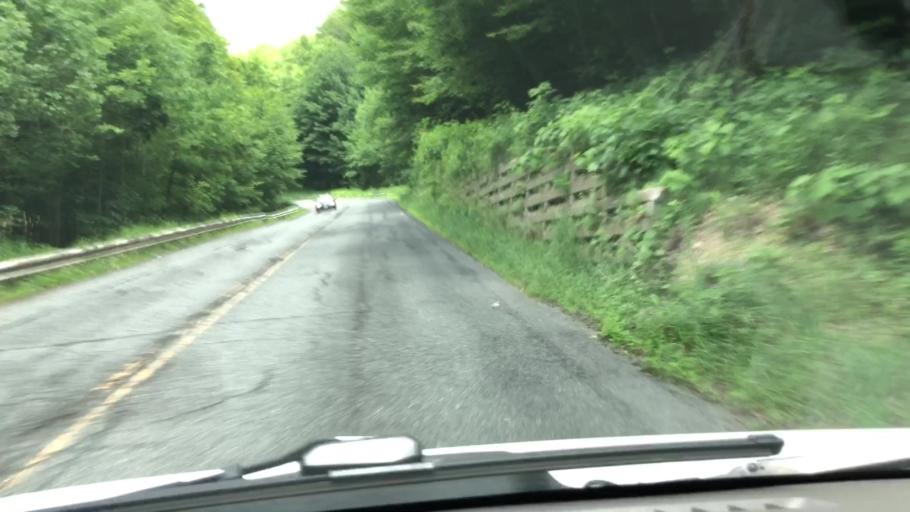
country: US
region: Massachusetts
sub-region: Berkshire County
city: Adams
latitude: 42.5815
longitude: -73.0903
